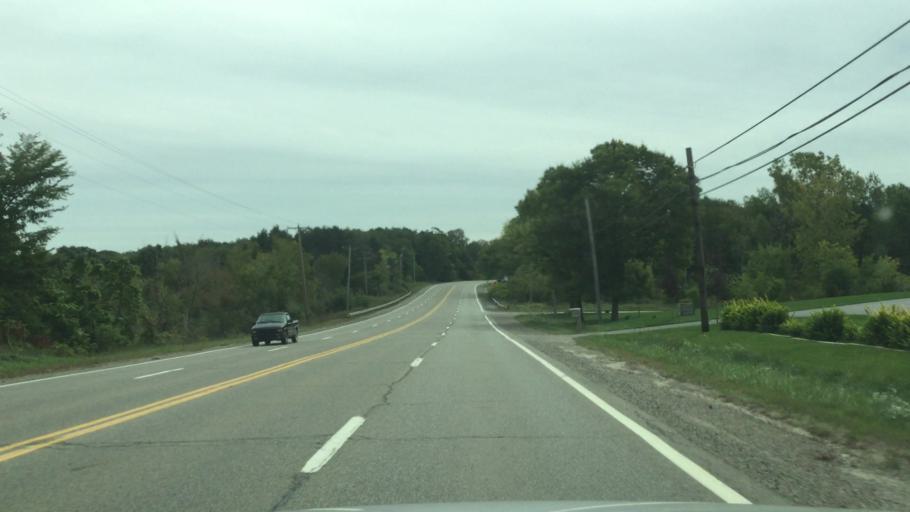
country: US
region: Michigan
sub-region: Oakland County
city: Holly
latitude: 42.8118
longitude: -83.5412
